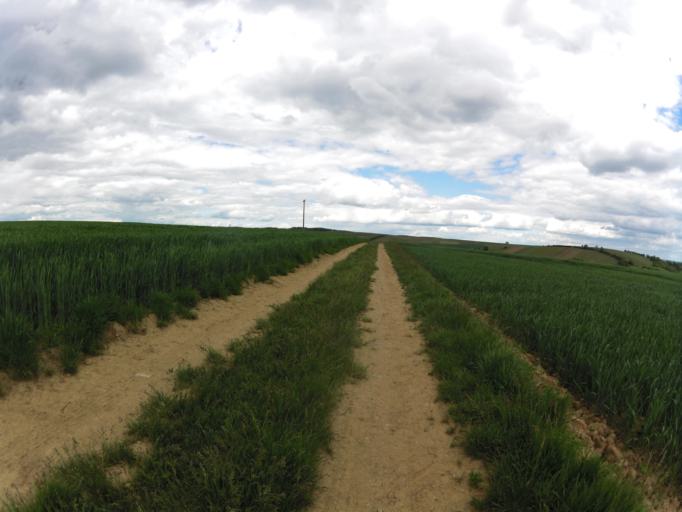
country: DE
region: Bavaria
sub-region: Regierungsbezirk Unterfranken
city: Volkach
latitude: 49.8768
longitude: 10.2415
